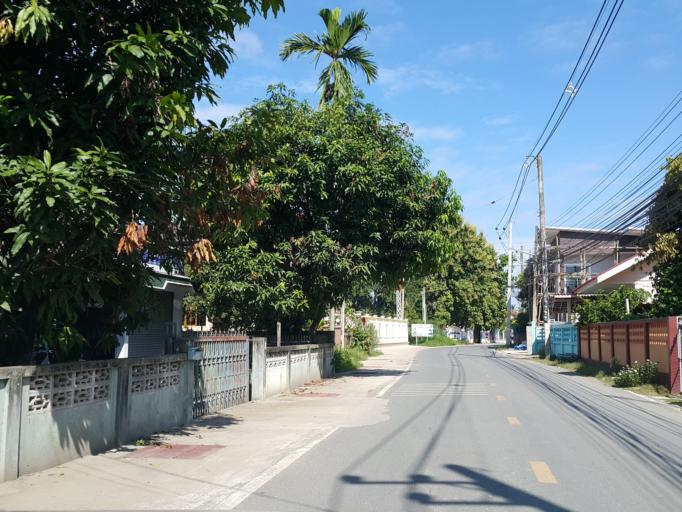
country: TH
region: Chiang Mai
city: San Sai
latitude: 18.7901
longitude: 99.0470
